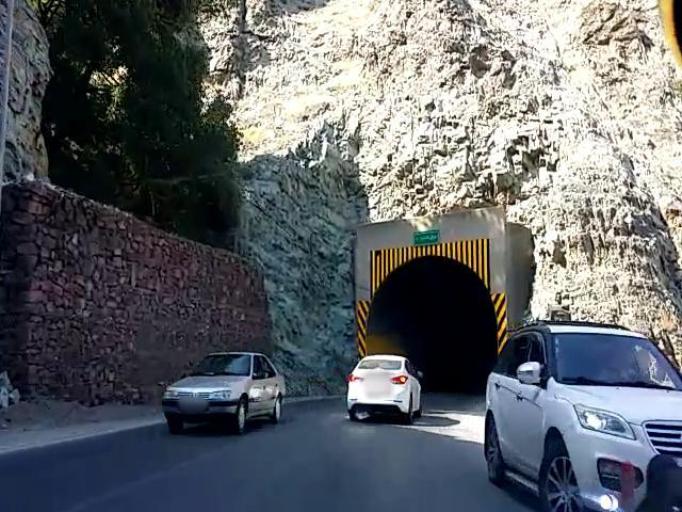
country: IR
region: Alborz
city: Karaj
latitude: 36.0107
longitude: 51.1231
